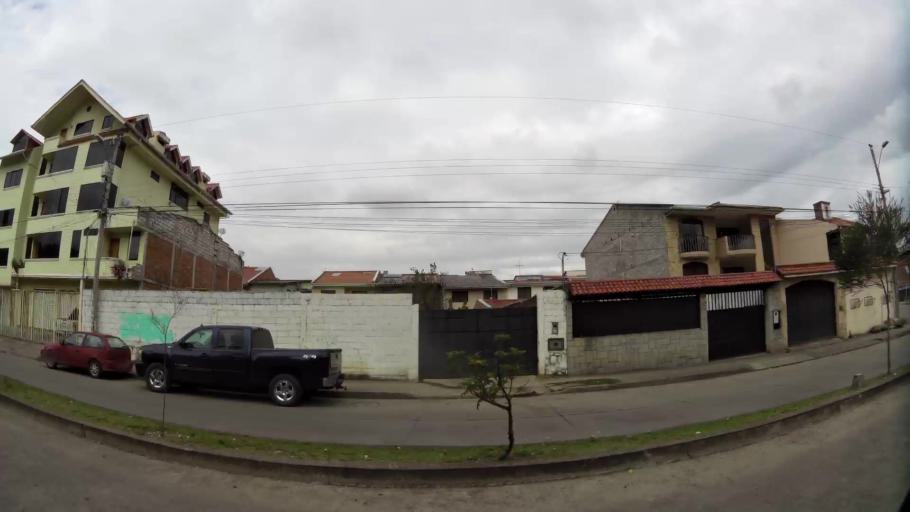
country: EC
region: Azuay
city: Cuenca
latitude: -2.9015
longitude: -78.9800
